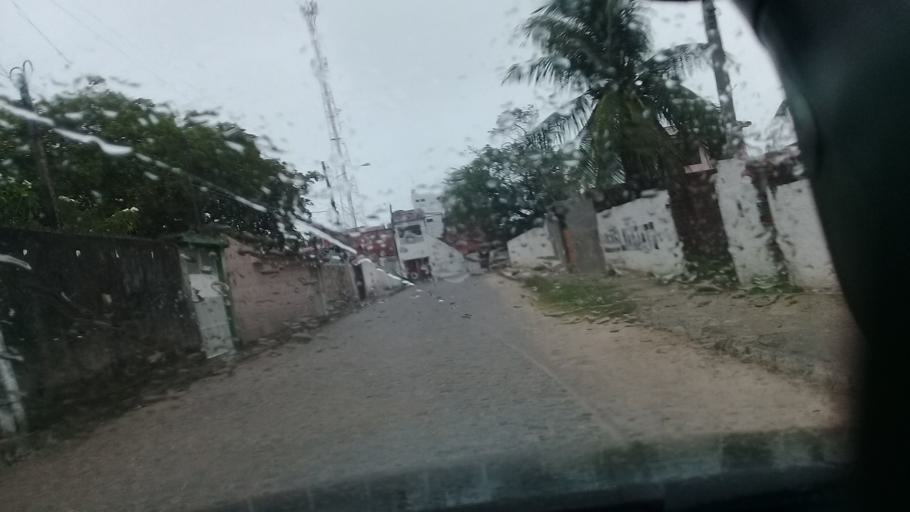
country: BR
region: Pernambuco
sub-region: Itamaraca
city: Itamaraca
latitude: -7.7435
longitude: -34.8263
